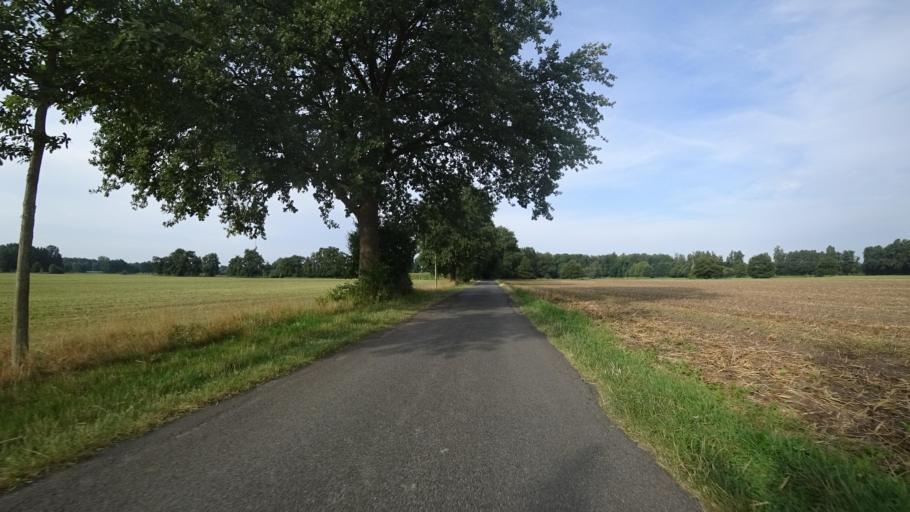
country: DE
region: North Rhine-Westphalia
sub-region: Regierungsbezirk Detmold
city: Steinhagen
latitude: 51.9553
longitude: 8.4331
